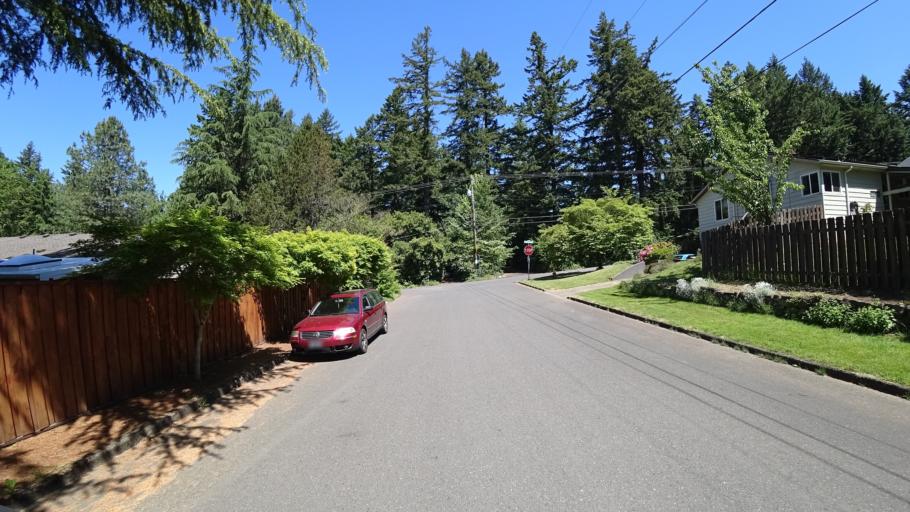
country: US
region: Oregon
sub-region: Washington County
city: Raleigh Hills
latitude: 45.4903
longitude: -122.7168
